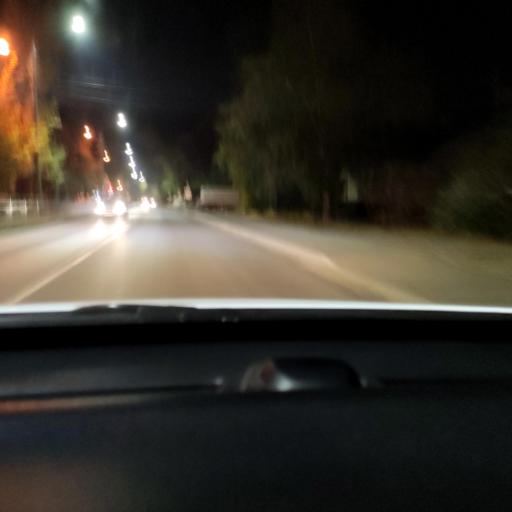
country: RU
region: Voronezj
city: Somovo
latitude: 51.7341
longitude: 39.2668
